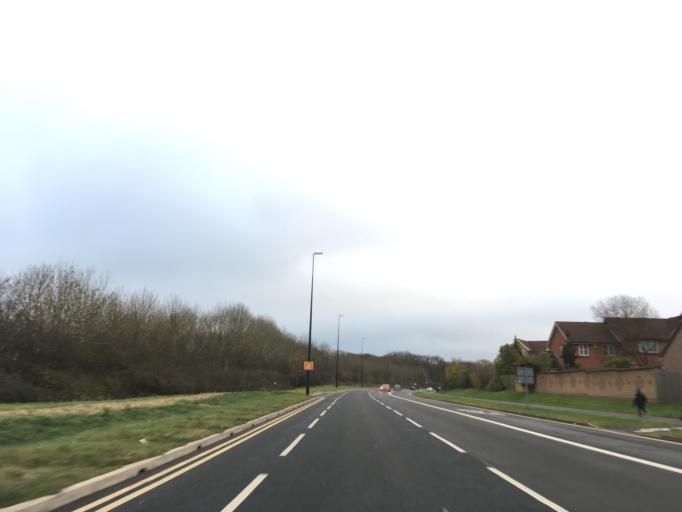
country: GB
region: England
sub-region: South Gloucestershire
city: Almondsbury
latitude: 51.5397
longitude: -2.5521
